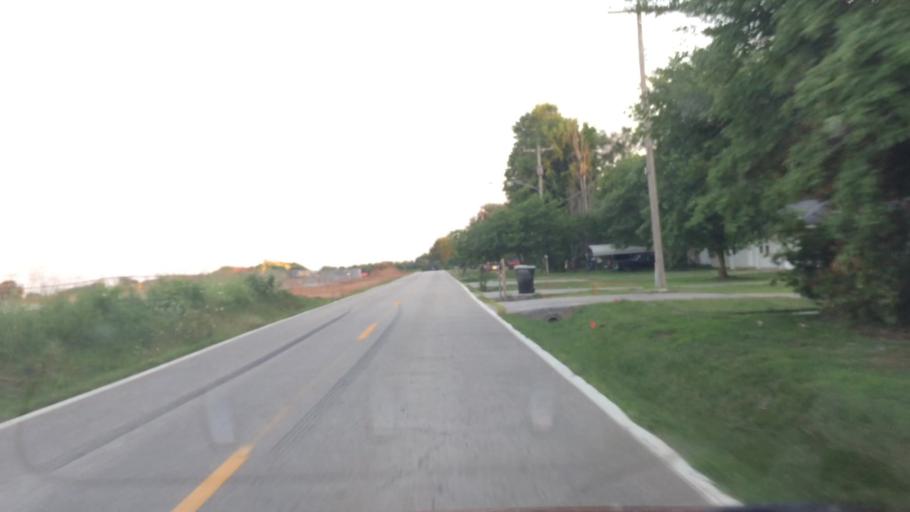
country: US
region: Missouri
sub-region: Greene County
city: Springfield
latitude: 37.2045
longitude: -93.3742
